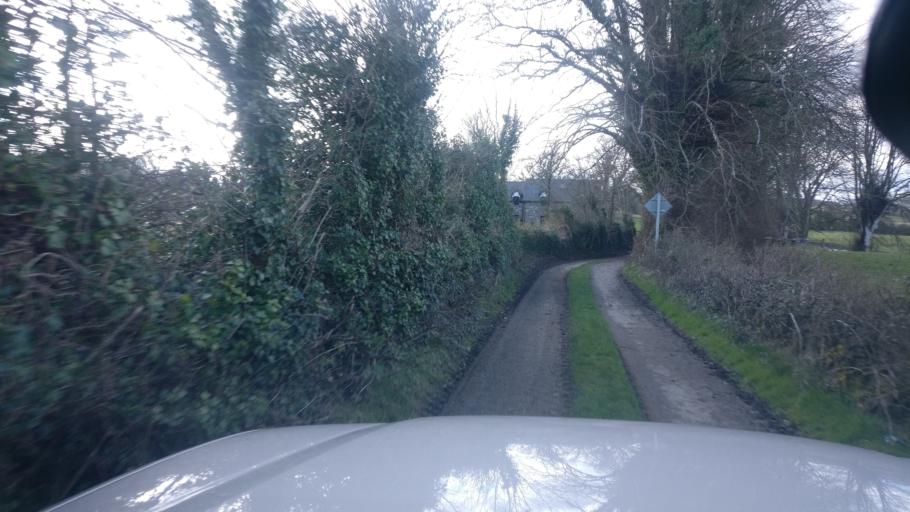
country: IE
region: Connaught
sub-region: County Galway
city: Loughrea
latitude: 53.1828
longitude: -8.4276
